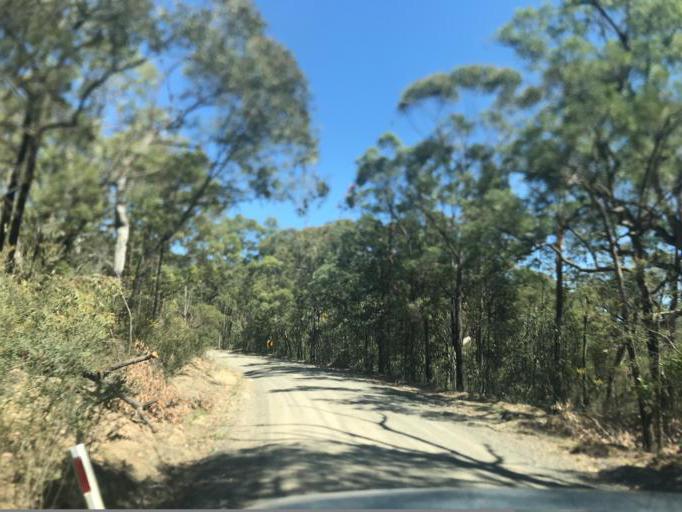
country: AU
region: New South Wales
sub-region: Wyong Shire
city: Little Jilliby
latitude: -33.1518
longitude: 151.0800
